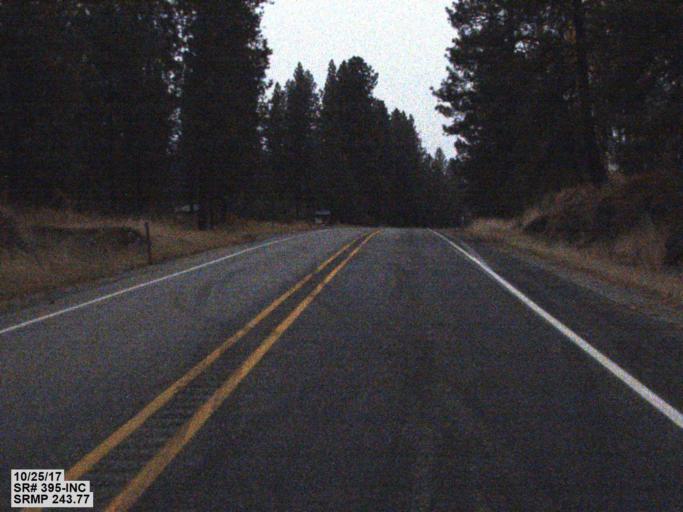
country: US
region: Washington
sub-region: Stevens County
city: Kettle Falls
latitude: 48.6526
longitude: -118.1137
